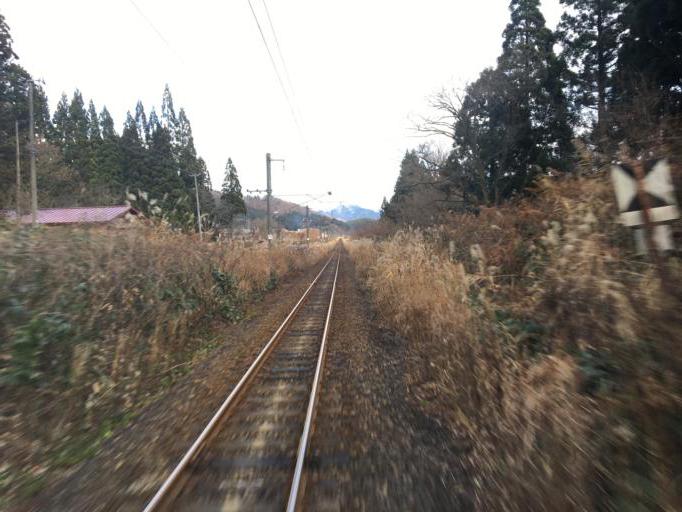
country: JP
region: Yamagata
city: Shinjo
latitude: 38.9642
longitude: 140.2950
